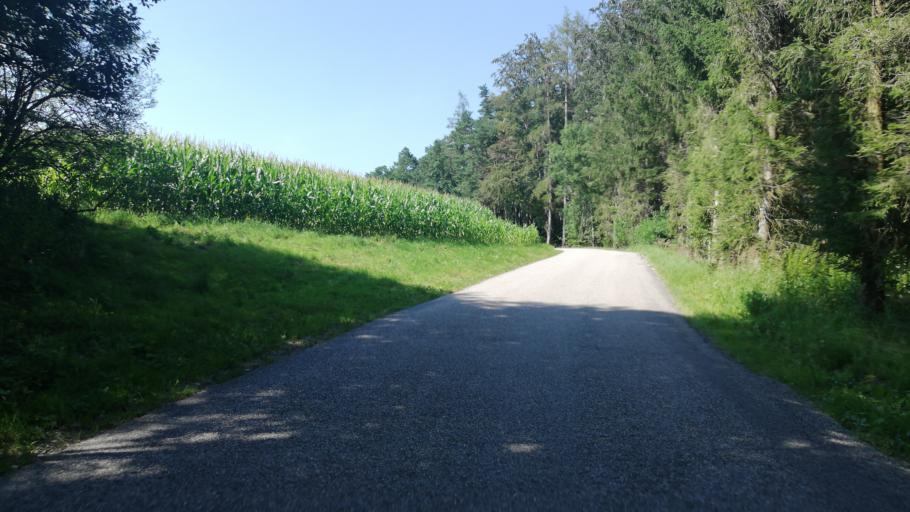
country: AT
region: Upper Austria
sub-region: Wels-Land
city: Pennewang
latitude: 48.1598
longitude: 13.8627
